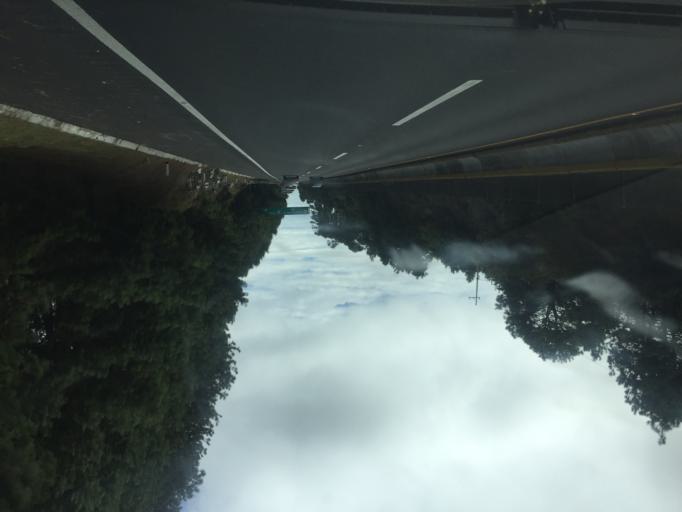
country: MX
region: Morelos
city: Tres Marias
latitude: 19.0786
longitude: -99.2331
